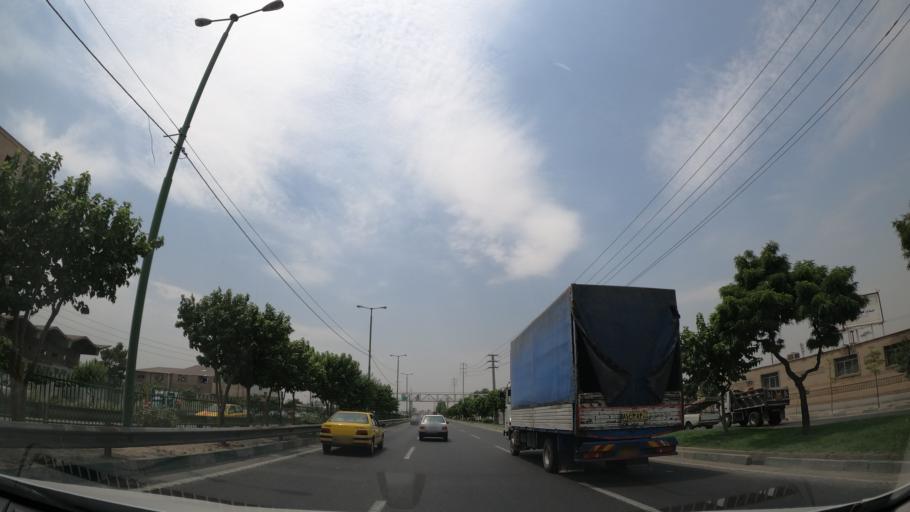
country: IR
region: Tehran
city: Eslamshahr
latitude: 35.6766
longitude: 51.2838
